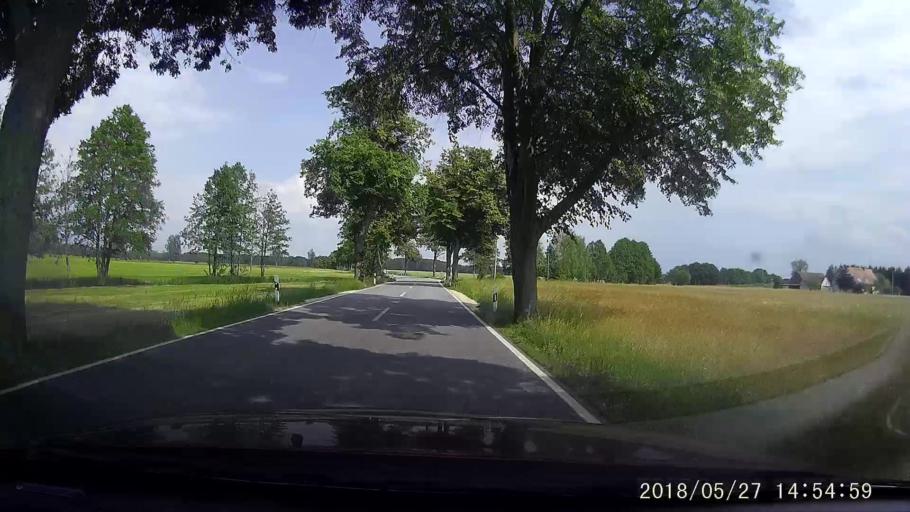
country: DE
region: Saxony
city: Klitten
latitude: 51.3477
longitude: 14.6087
